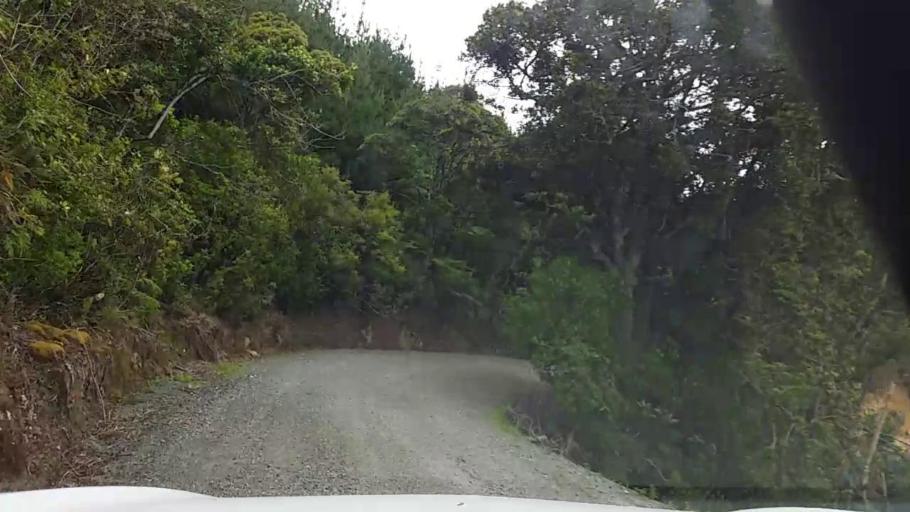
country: NZ
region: Northland
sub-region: Far North District
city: Kawakawa
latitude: -35.4609
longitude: 174.2627
